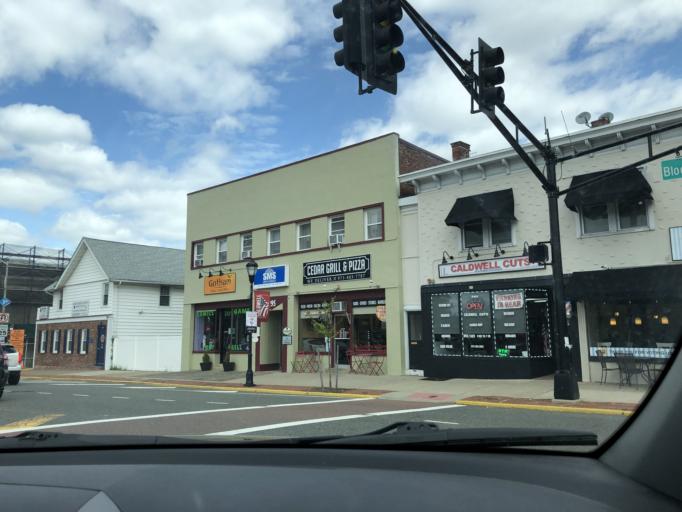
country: US
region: New Jersey
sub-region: Essex County
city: Caldwell
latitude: 40.8390
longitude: -74.2750
